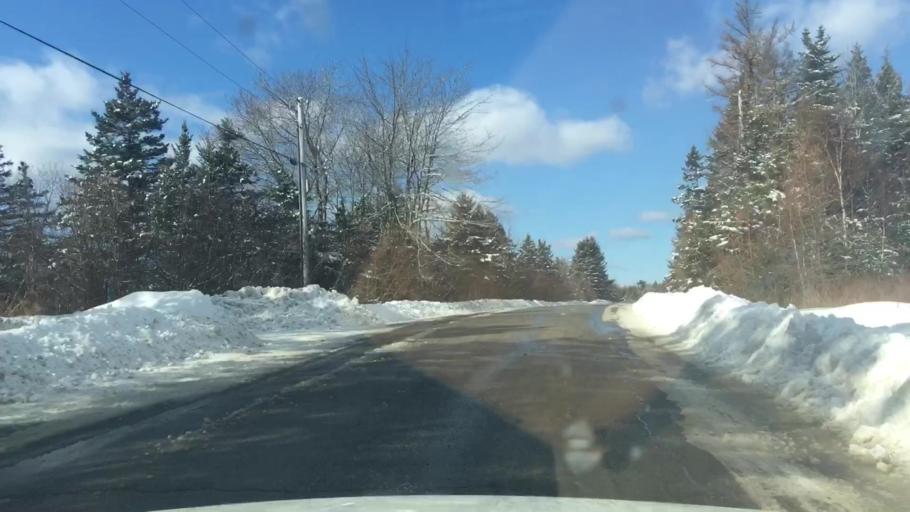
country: US
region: Maine
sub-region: Washington County
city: Machias
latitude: 44.6807
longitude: -67.4555
